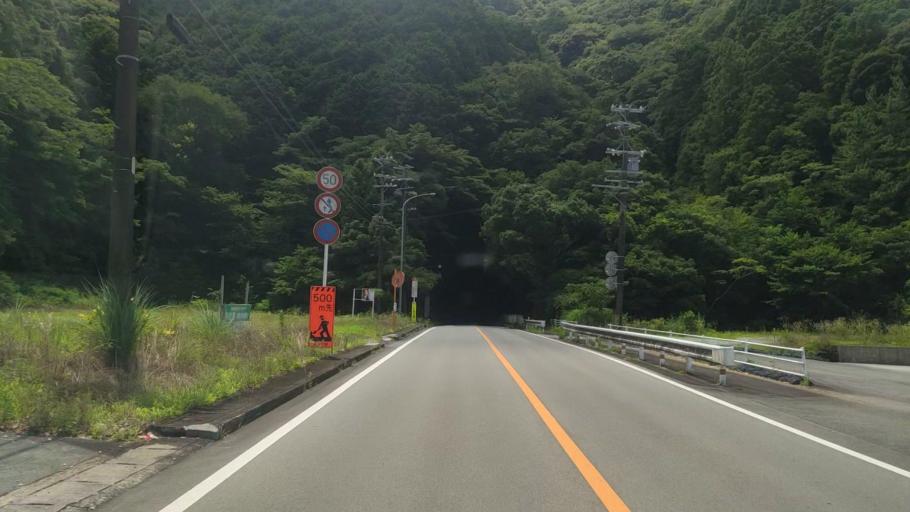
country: JP
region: Mie
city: Ise
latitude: 34.2729
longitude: 136.4913
